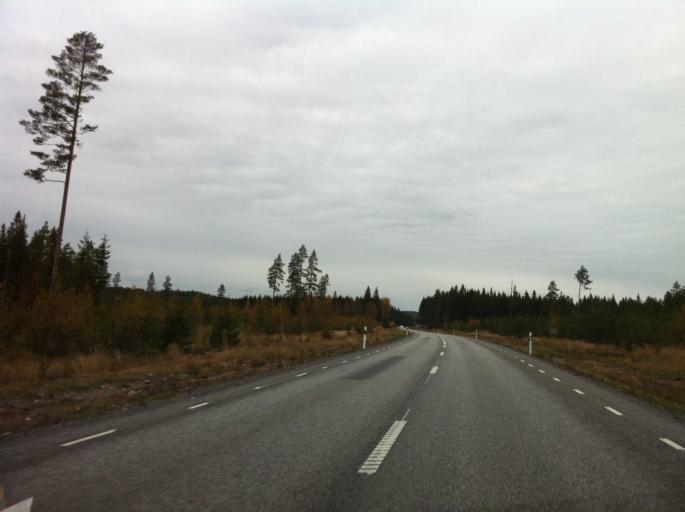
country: SE
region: OErebro
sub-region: Ljusnarsbergs Kommun
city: Kopparberg
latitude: 59.9588
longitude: 15.0207
